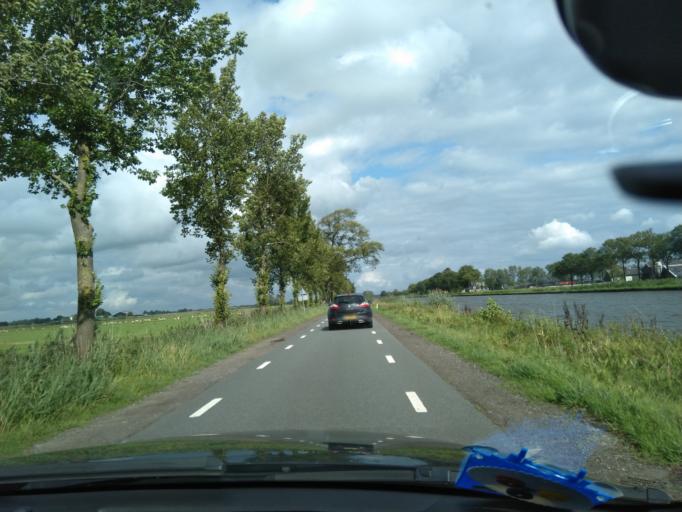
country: NL
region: Groningen
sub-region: Gemeente Zuidhorn
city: Grijpskerk
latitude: 53.2522
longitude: 6.3408
